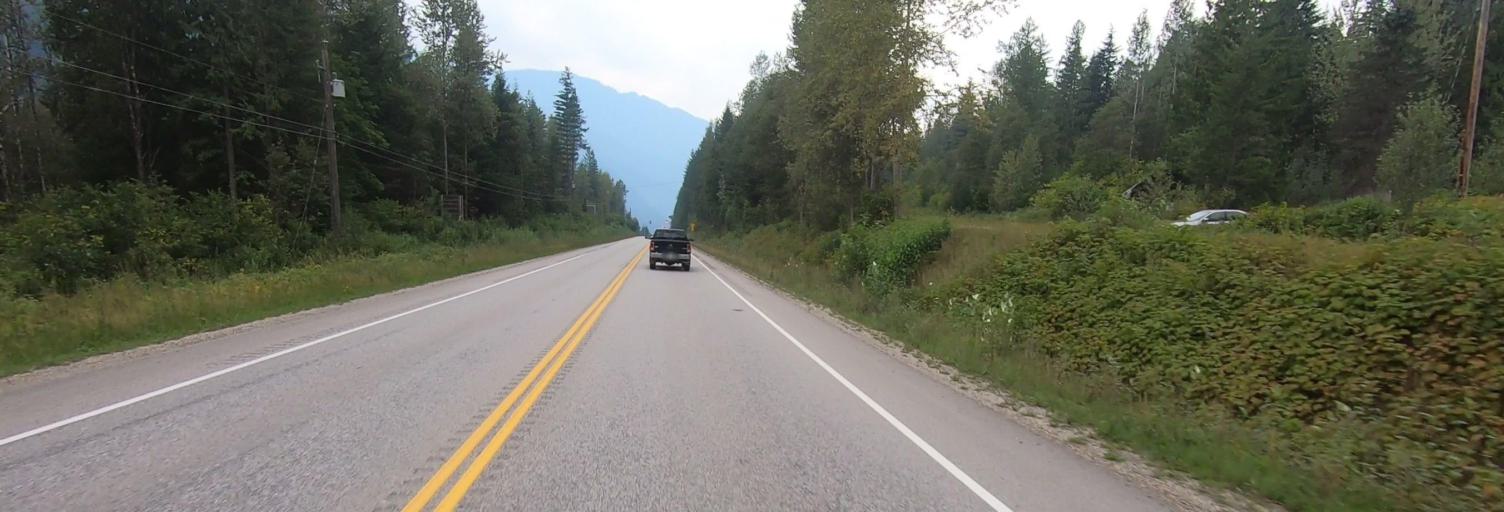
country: CA
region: British Columbia
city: Revelstoke
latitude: 50.9769
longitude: -118.5343
